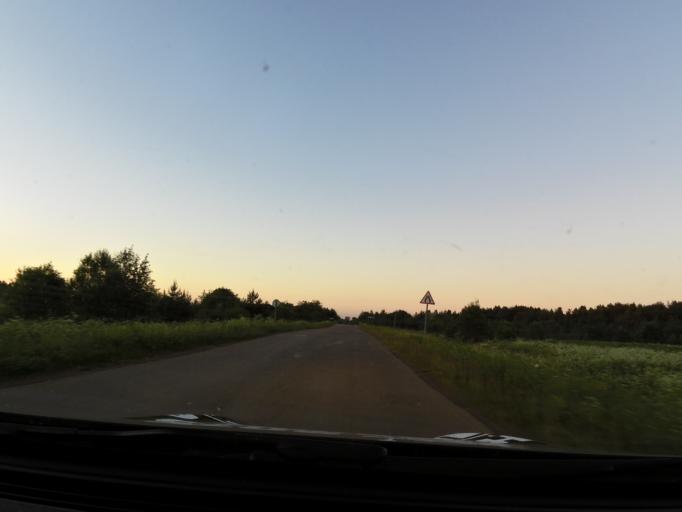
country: RU
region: Leningrad
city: Voznesen'ye
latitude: 60.8349
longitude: 35.7597
